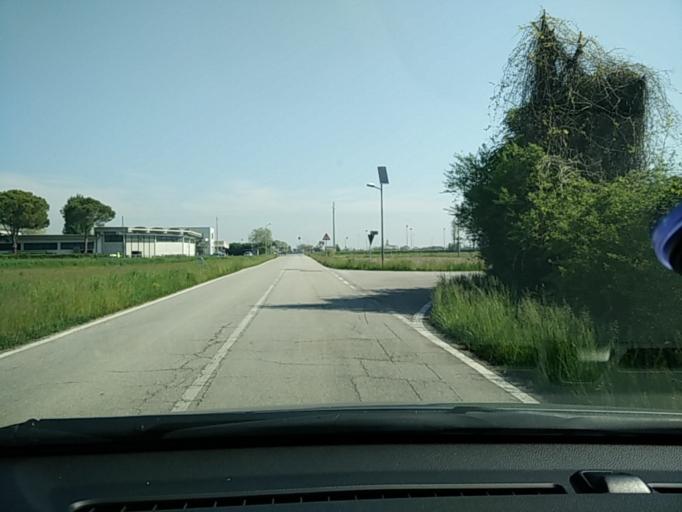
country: IT
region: Veneto
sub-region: Provincia di Treviso
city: Zenson di Piave
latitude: 45.6765
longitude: 12.4831
